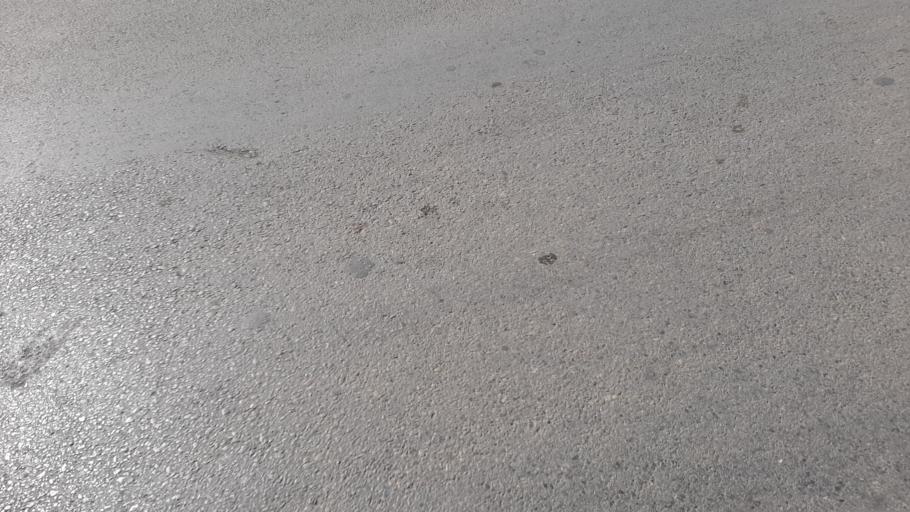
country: TN
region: Qabis
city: Gabes
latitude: 33.8679
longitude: 10.1034
